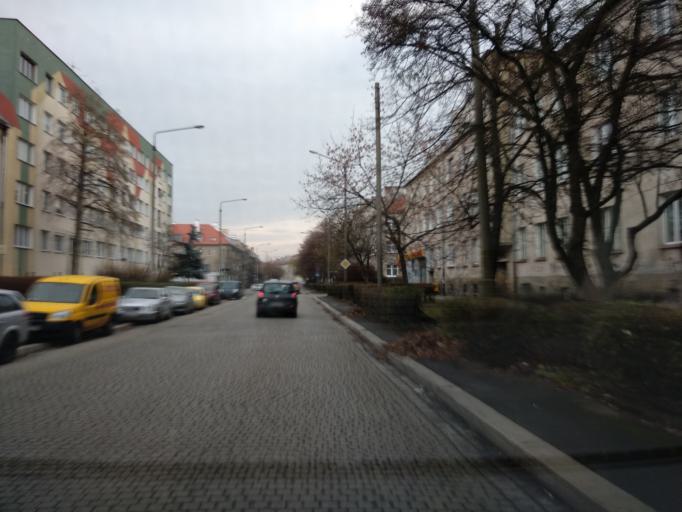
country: PL
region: Lower Silesian Voivodeship
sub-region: Powiat wroclawski
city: Wroclaw
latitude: 51.0937
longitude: 16.9990
